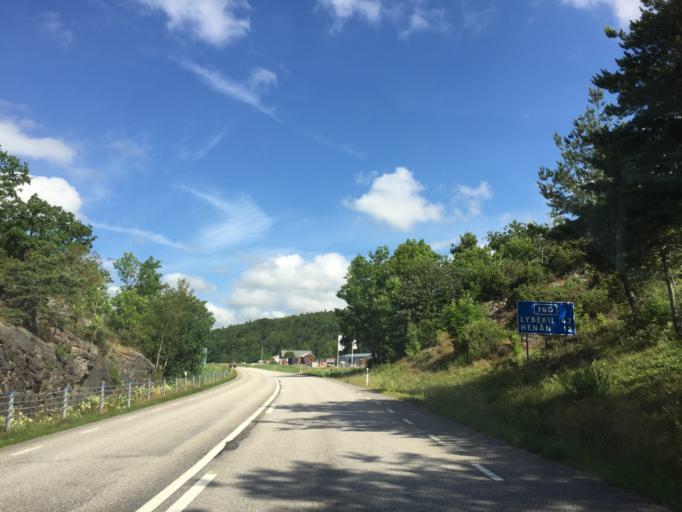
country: SE
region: Vaestra Goetaland
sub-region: Tjorns Kommun
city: Myggenas
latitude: 58.1279
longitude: 11.7222
